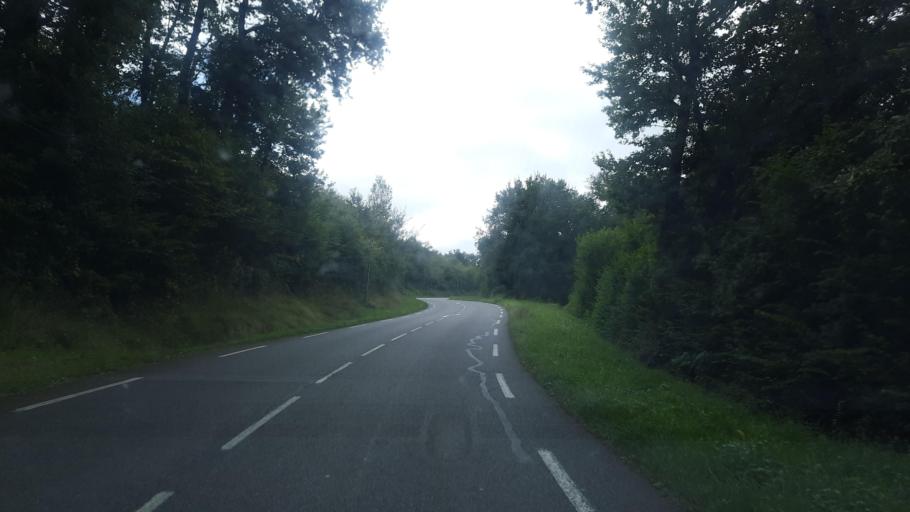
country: FR
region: Midi-Pyrenees
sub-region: Departement des Hautes-Pyrenees
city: Trie-sur-Baise
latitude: 43.3115
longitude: 0.3798
